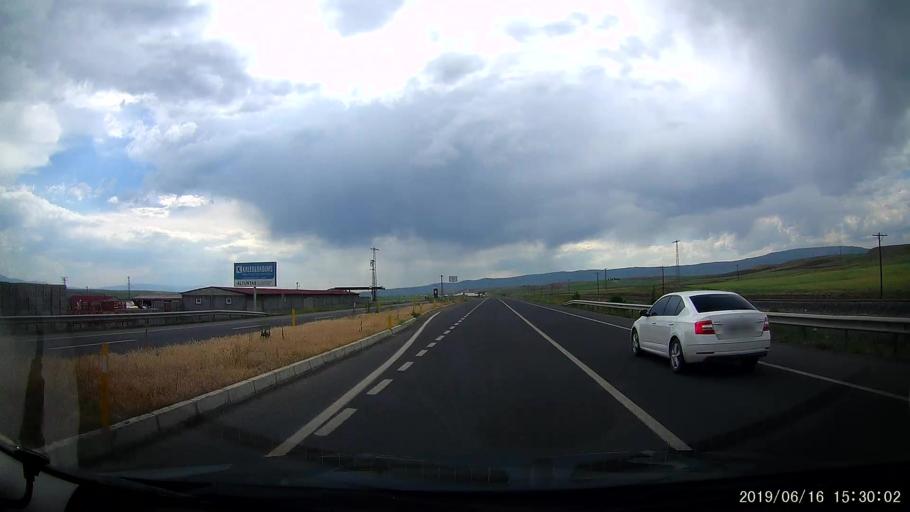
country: TR
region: Erzurum
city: Horasan
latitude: 40.0329
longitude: 42.1168
